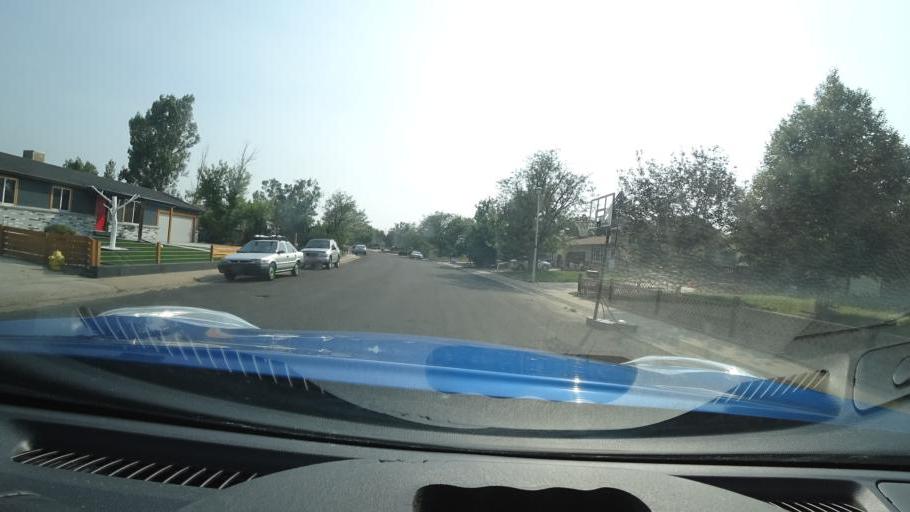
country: US
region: Colorado
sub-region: Adams County
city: Aurora
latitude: 39.6657
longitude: -104.8082
